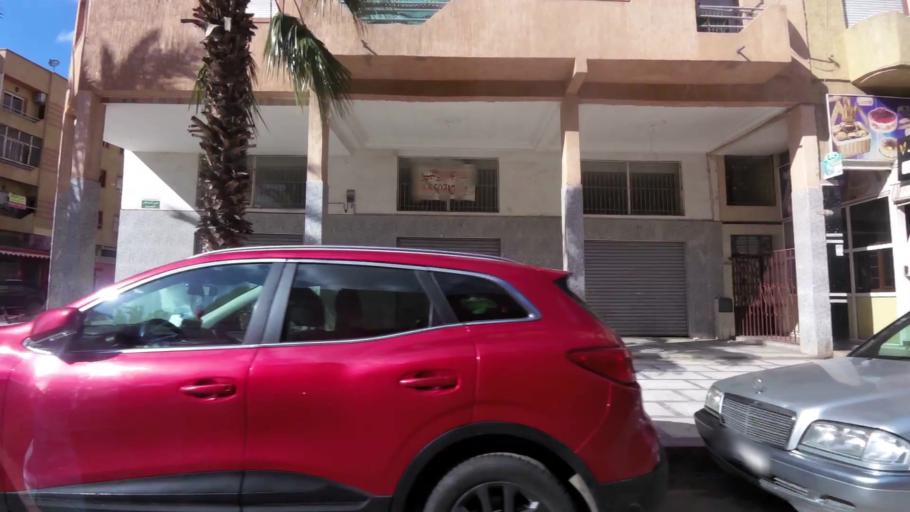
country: MA
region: Chaouia-Ouardigha
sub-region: Settat Province
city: Berrechid
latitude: 33.2748
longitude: -7.5796
